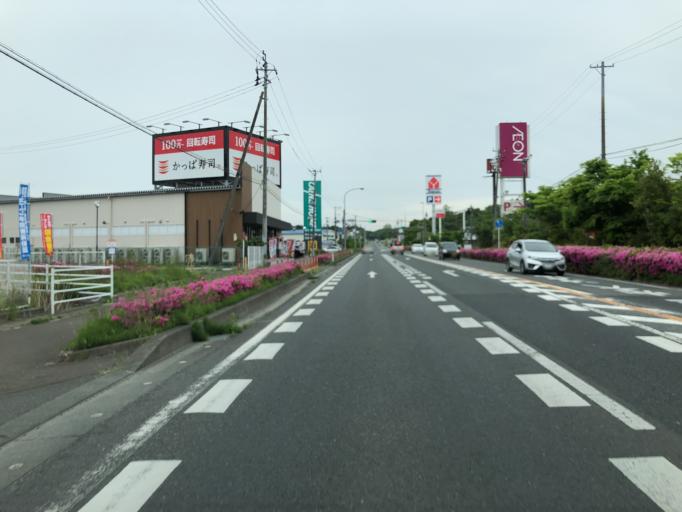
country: JP
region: Miyagi
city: Marumori
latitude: 37.7883
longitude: 140.9317
